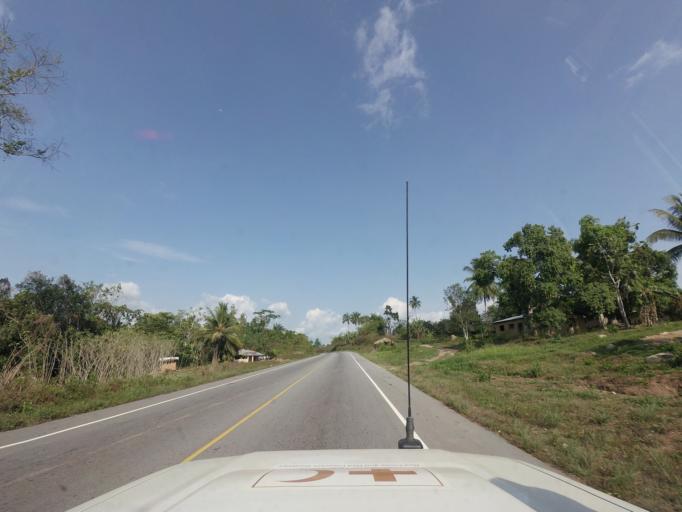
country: LR
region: Bong
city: Gbarnga
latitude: 6.8481
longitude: -9.8011
